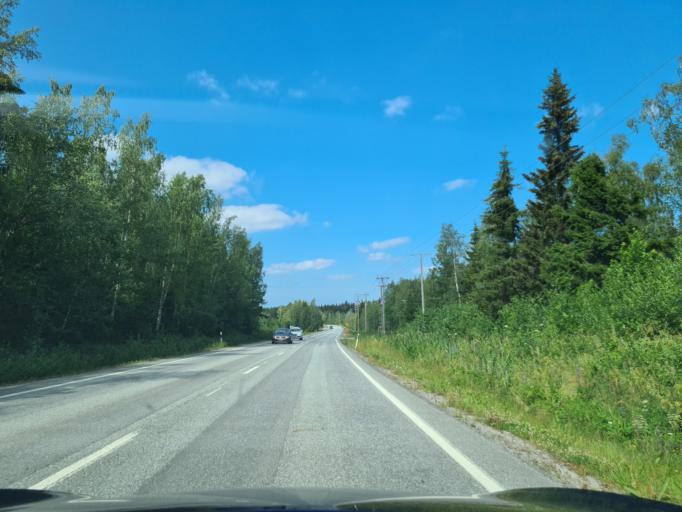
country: FI
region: Ostrobothnia
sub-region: Vaasa
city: Vaasa
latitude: 63.1857
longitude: 21.5667
